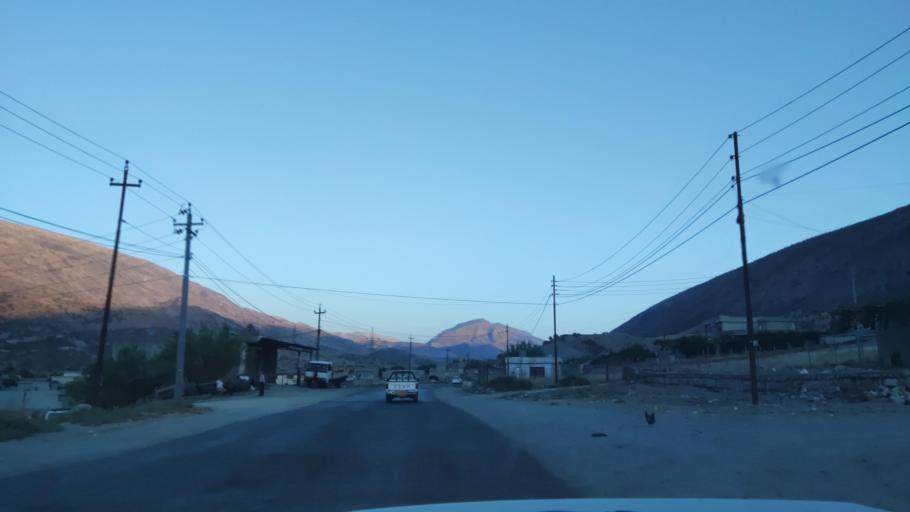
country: IQ
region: Arbil
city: Ruwandiz
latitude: 36.5879
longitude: 44.3939
